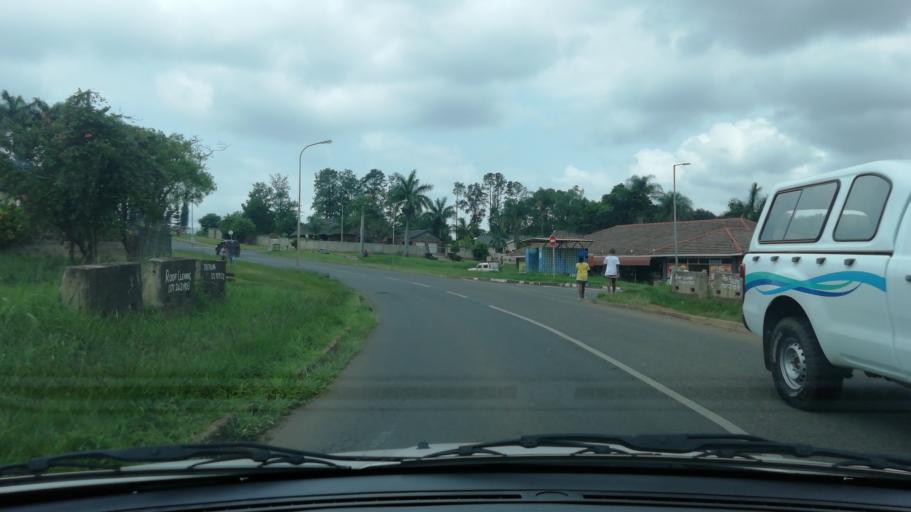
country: ZA
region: KwaZulu-Natal
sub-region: uThungulu District Municipality
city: Empangeni
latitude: -28.7577
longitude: 31.8917
